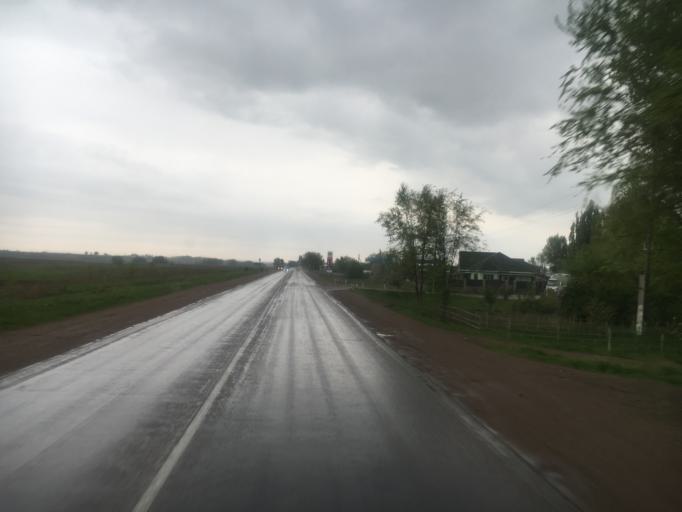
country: KZ
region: Almaty Oblysy
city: Burunday
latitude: 43.2883
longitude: 76.6735
